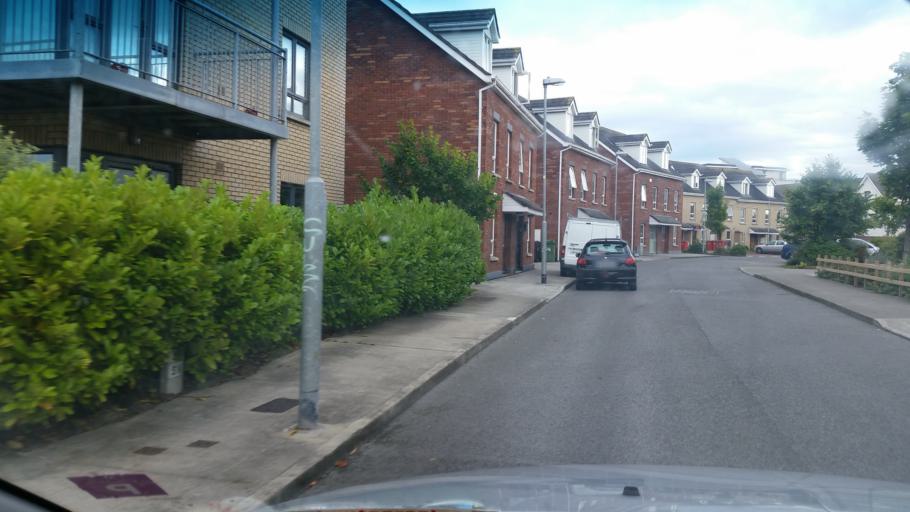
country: IE
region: Leinster
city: Donaghmede
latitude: 53.3998
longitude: -6.1503
